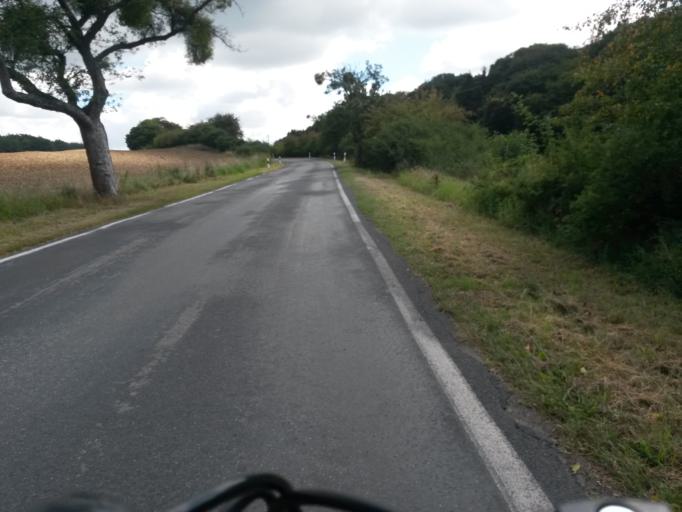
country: DE
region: Brandenburg
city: Althuttendorf
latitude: 53.0062
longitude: 13.8958
